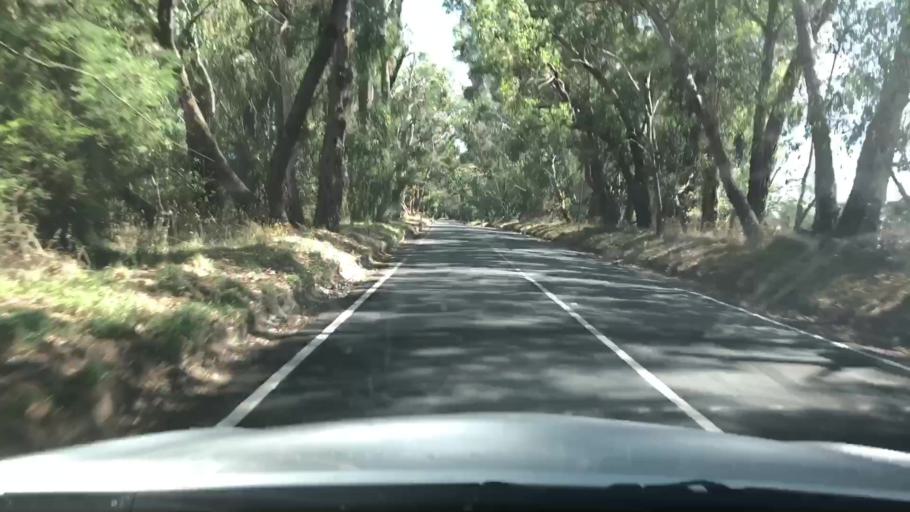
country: AU
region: Victoria
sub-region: Yarra Ranges
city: Woori Yallock
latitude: -37.8154
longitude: 145.4998
